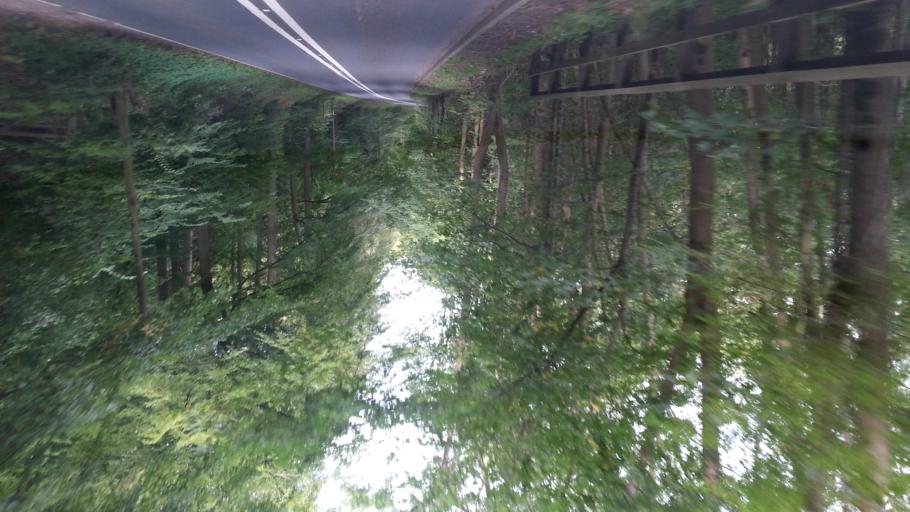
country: GB
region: England
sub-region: Gloucestershire
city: Painswick
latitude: 51.8177
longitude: -2.1700
